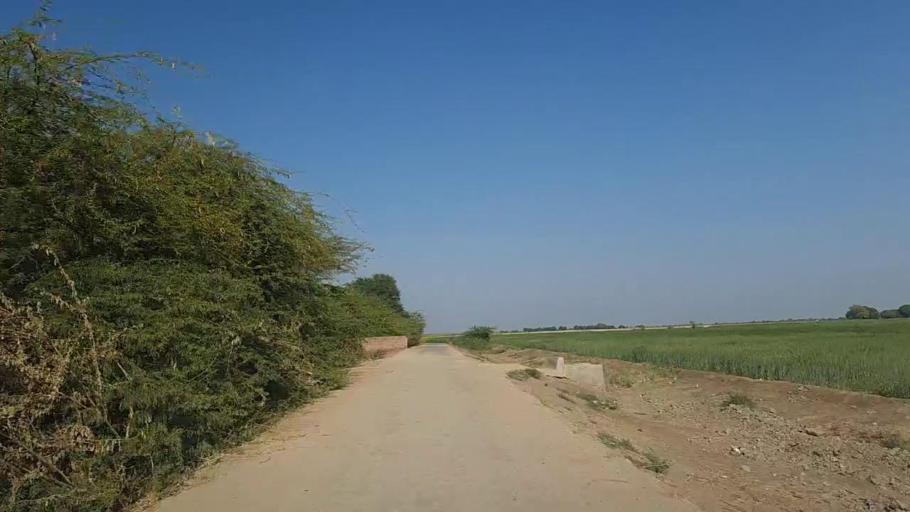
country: PK
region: Sindh
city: Digri
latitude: 25.0945
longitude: 69.2063
